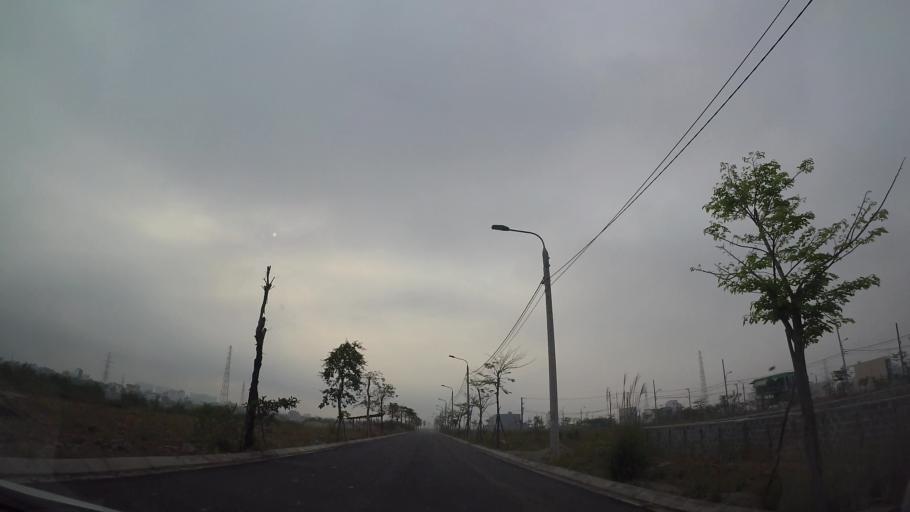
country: VN
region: Da Nang
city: Ngu Hanh Son
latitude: 16.0243
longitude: 108.2354
